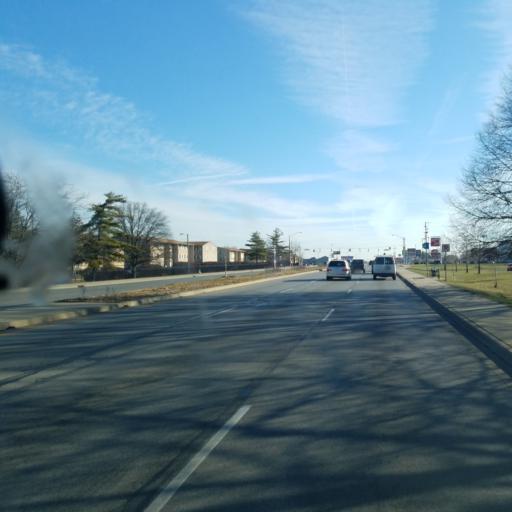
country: US
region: Indiana
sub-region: Marion County
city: Speedway
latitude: 39.8236
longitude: -86.2624
